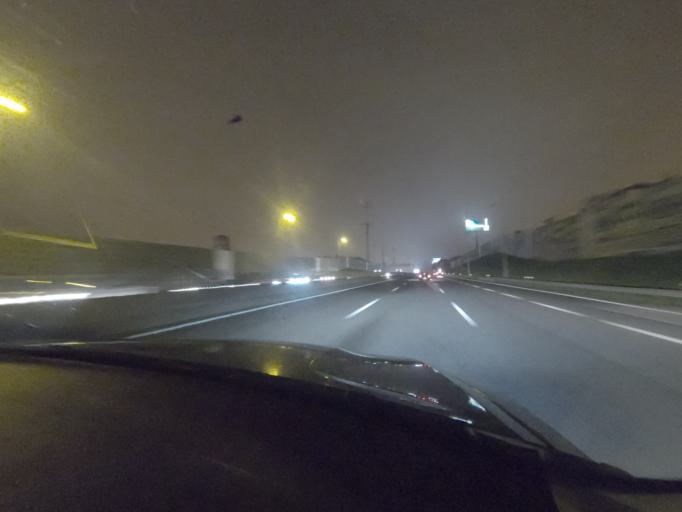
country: PT
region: Lisbon
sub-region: Loures
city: Santa Iria da Azoia
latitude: 38.8461
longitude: -9.0910
